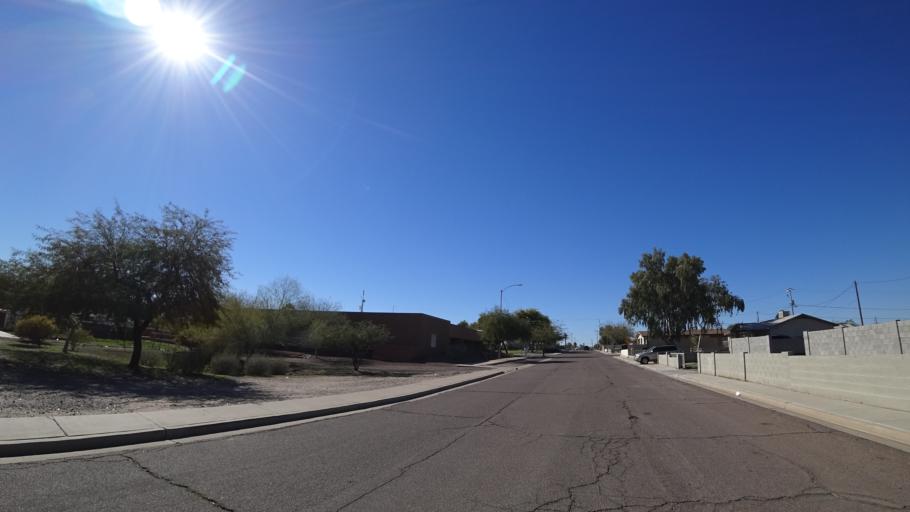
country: US
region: Arizona
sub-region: Maricopa County
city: Avondale
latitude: 33.4245
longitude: -112.3452
